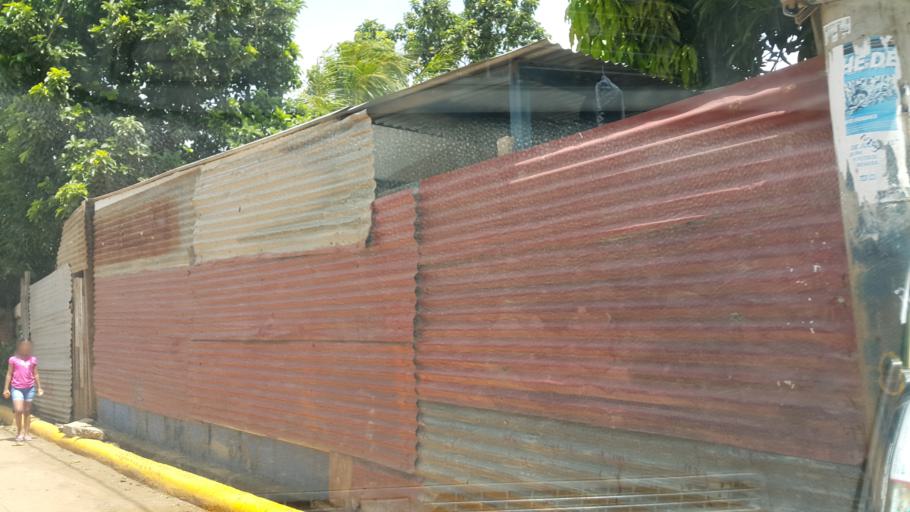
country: NI
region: Managua
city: Managua
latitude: 12.1154
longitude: -86.2425
